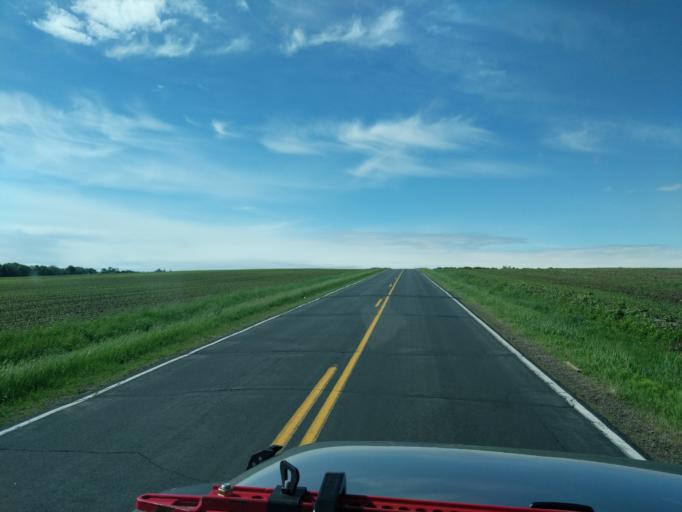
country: US
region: Wisconsin
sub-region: Saint Croix County
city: Hammond
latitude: 44.8765
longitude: -92.4966
